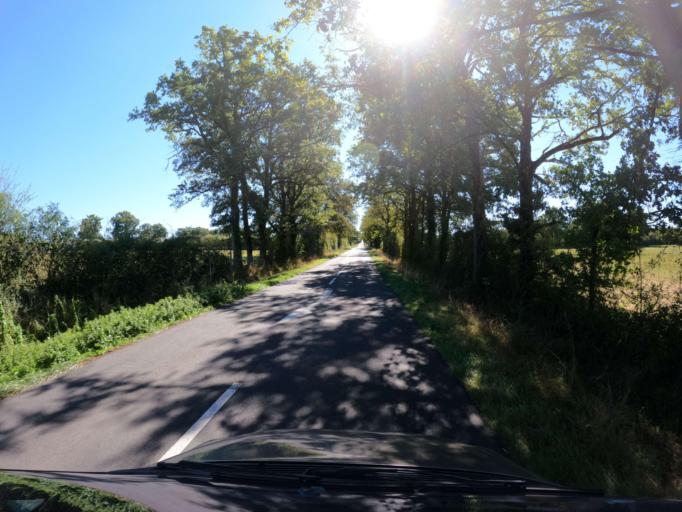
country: FR
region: Poitou-Charentes
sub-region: Departement de la Vienne
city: Lathus-Saint-Remy
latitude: 46.3286
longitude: 0.9651
